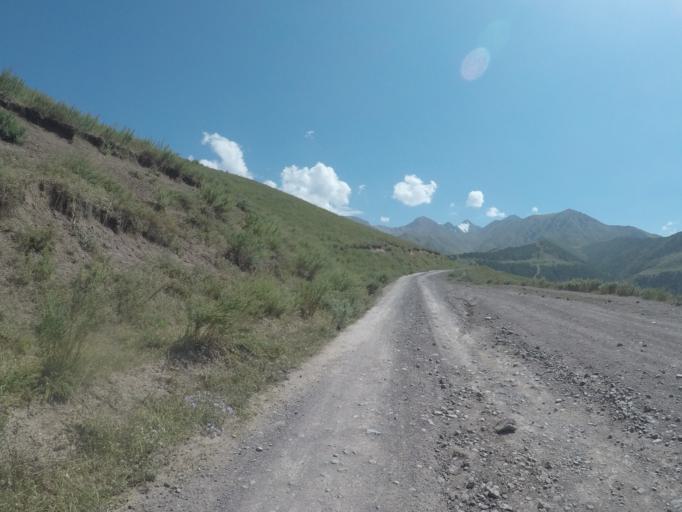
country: KG
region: Chuy
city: Bishkek
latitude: 42.6497
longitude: 74.5210
